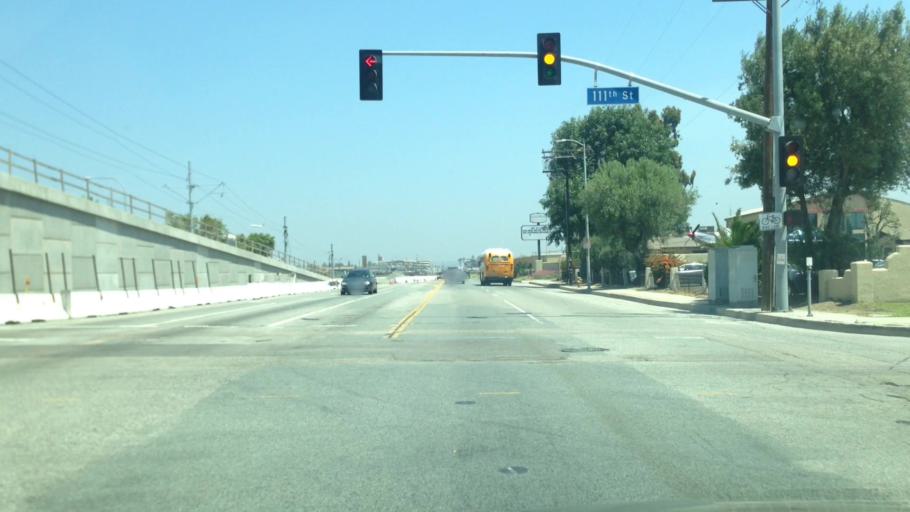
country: US
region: California
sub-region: Los Angeles County
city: Del Aire
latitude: 33.9343
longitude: -118.3785
